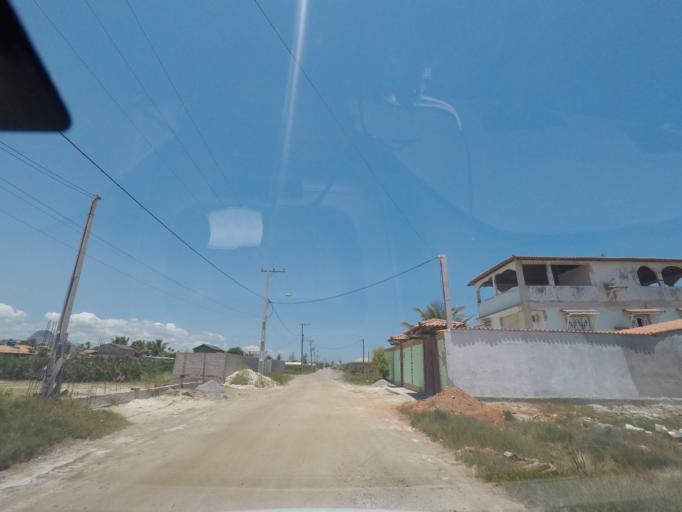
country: BR
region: Rio de Janeiro
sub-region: Niteroi
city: Niteroi
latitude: -22.9683
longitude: -42.9752
